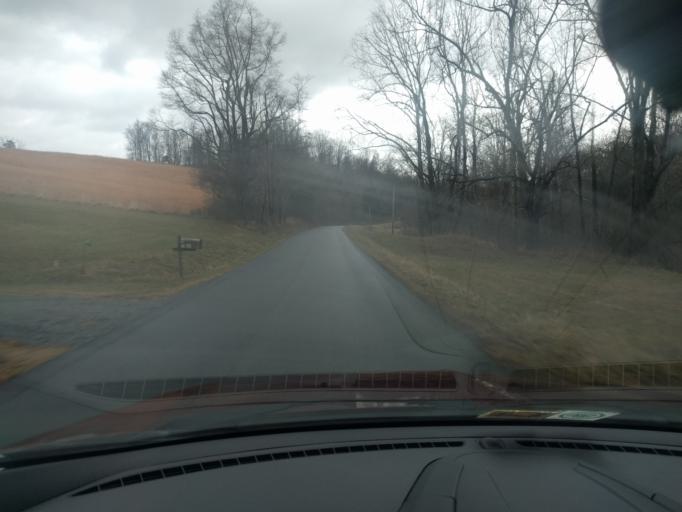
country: US
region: Virginia
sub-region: Botetourt County
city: Fincastle
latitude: 37.5984
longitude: -79.8510
